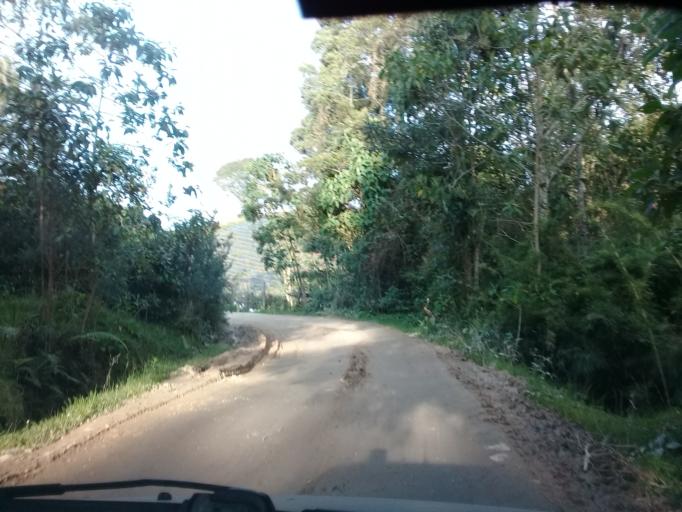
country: CO
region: Cundinamarca
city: Sibate
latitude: 4.4356
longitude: -74.2818
